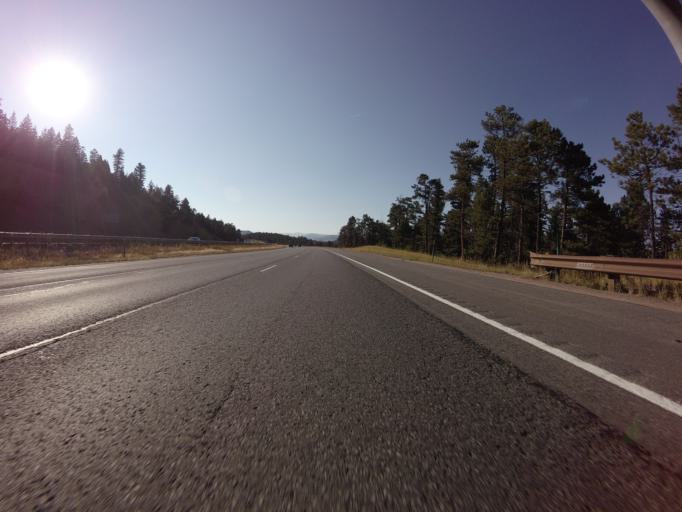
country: US
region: Colorado
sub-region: Jefferson County
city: Kittredge
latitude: 39.7093
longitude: -105.3484
